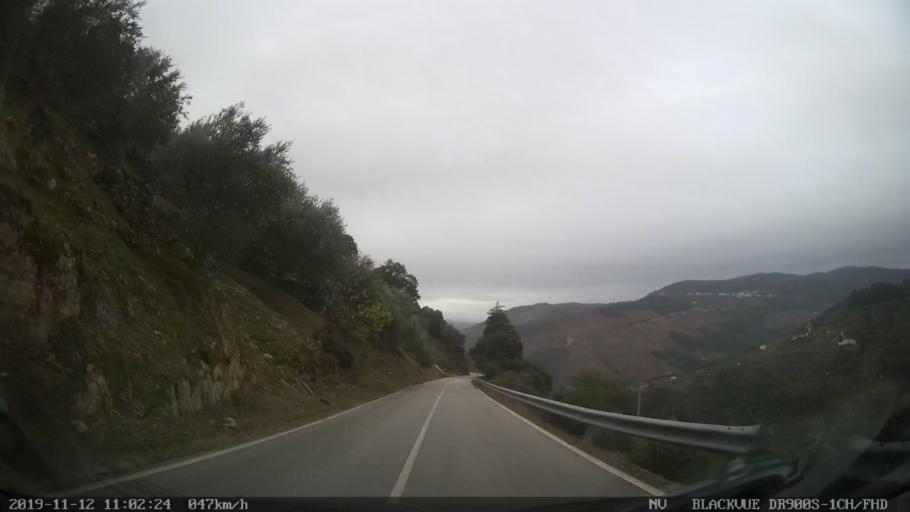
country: PT
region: Vila Real
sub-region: Sabrosa
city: Vilela
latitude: 41.2033
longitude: -7.5360
